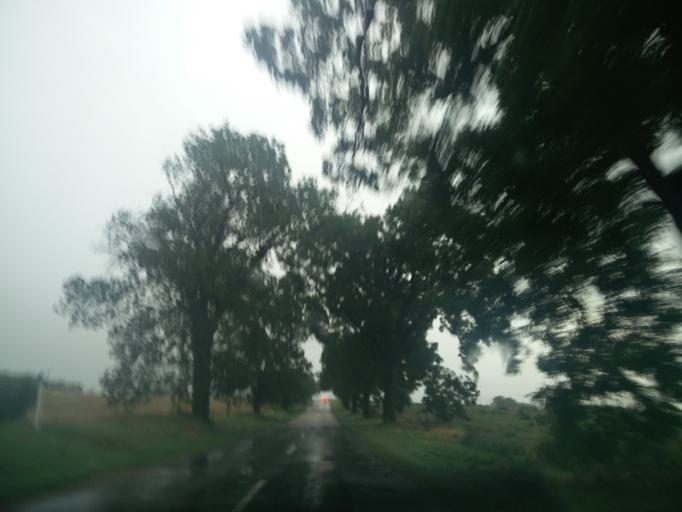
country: HU
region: Fejer
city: Bicske
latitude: 47.4313
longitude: 18.6270
